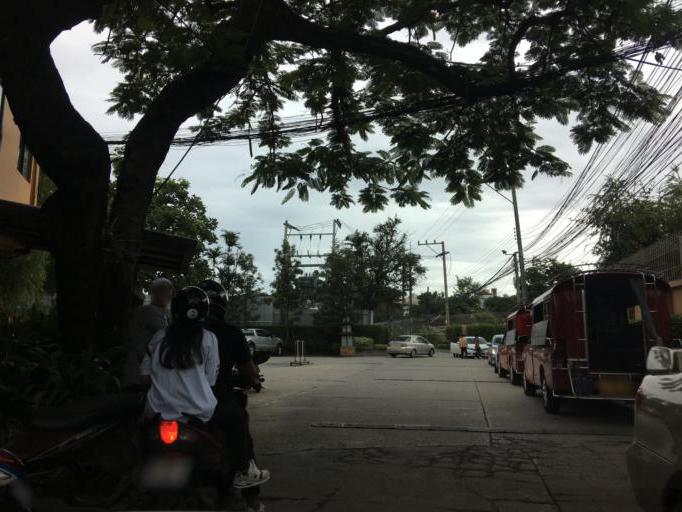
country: TH
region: Chiang Mai
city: Chiang Mai
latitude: 18.8058
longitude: 98.9637
